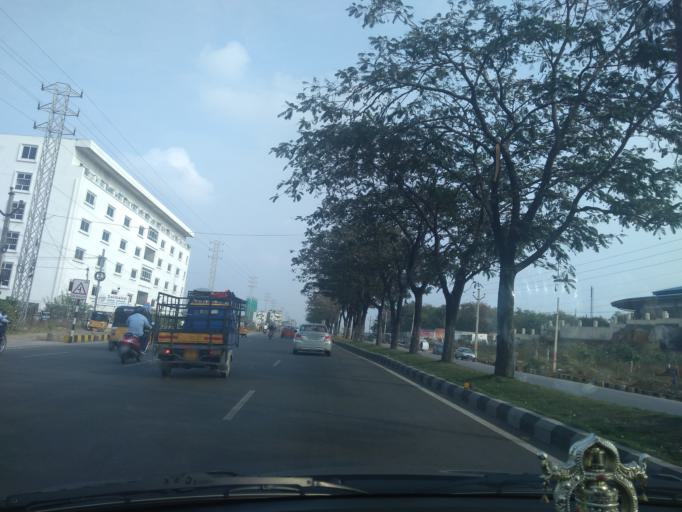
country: IN
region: Telangana
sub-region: Rangareddi
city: Balapur
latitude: 17.3169
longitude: 78.4396
